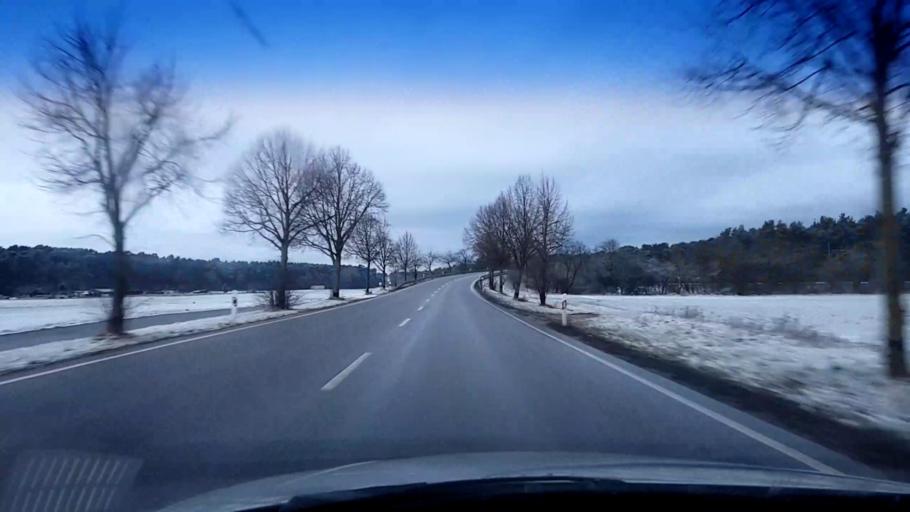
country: DE
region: Bavaria
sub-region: Upper Franconia
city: Hirschaid
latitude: 49.8240
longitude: 10.9840
